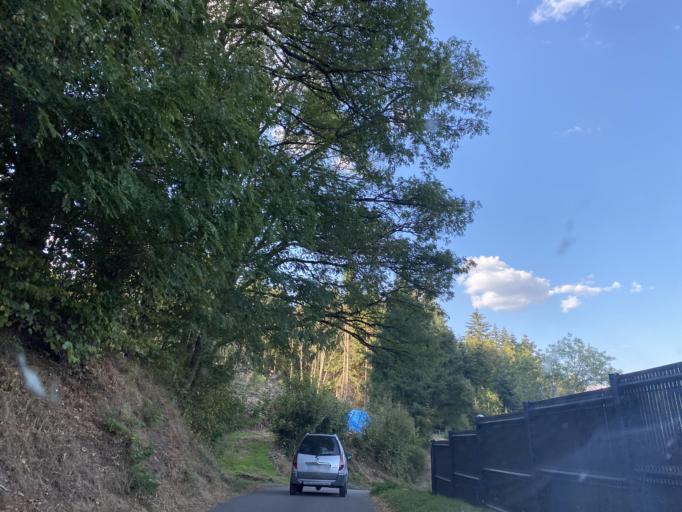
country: FR
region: Rhone-Alpes
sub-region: Departement de la Loire
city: Noiretable
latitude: 45.8109
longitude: 3.7532
